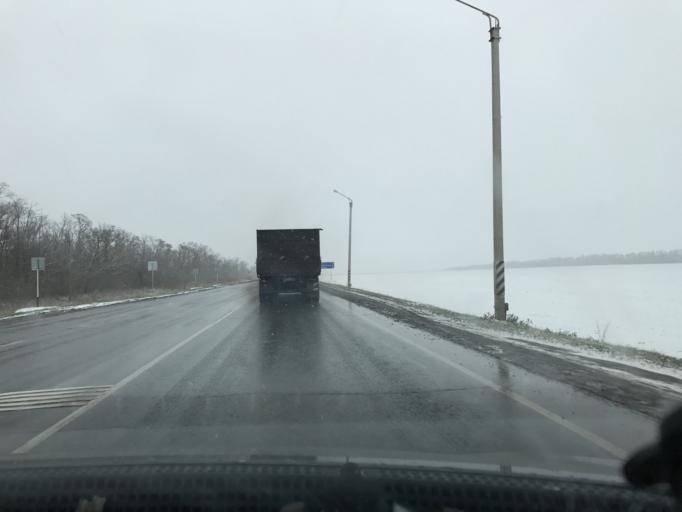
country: RU
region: Rostov
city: Yegorlykskaya
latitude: 46.5846
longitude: 40.6322
